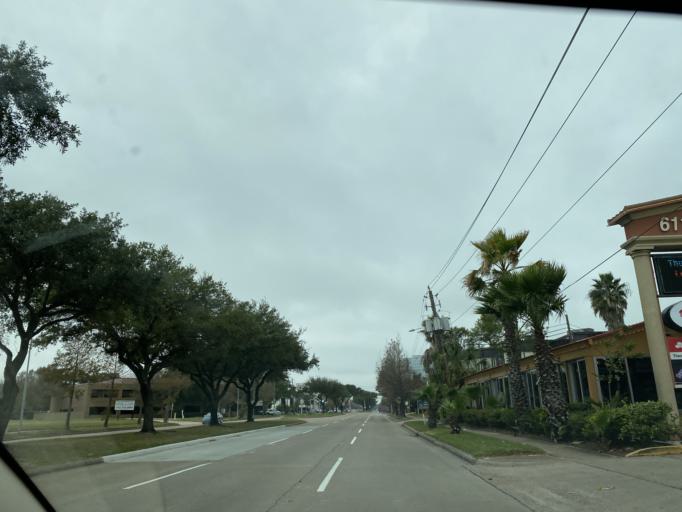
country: US
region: Texas
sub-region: Harris County
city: Bellaire
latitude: 29.7319
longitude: -95.4875
